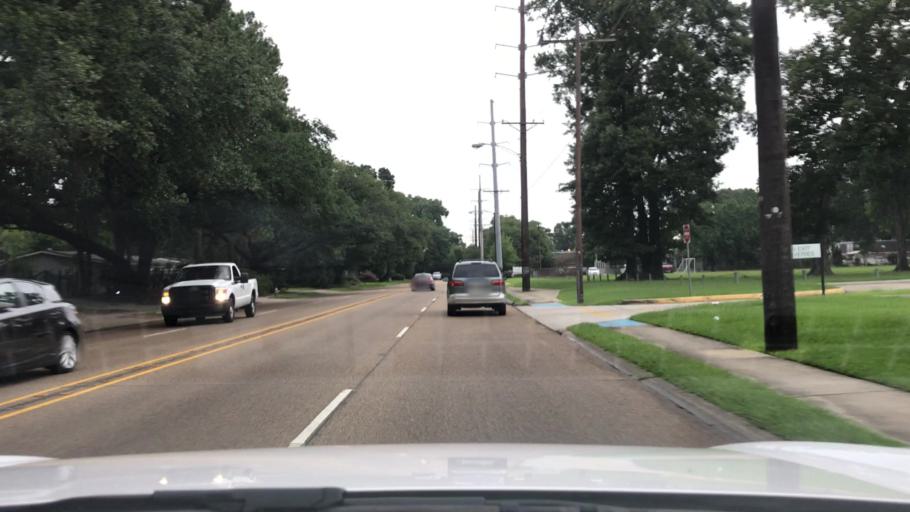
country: US
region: Louisiana
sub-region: East Baton Rouge Parish
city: Baton Rouge
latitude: 30.4313
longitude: -91.1352
